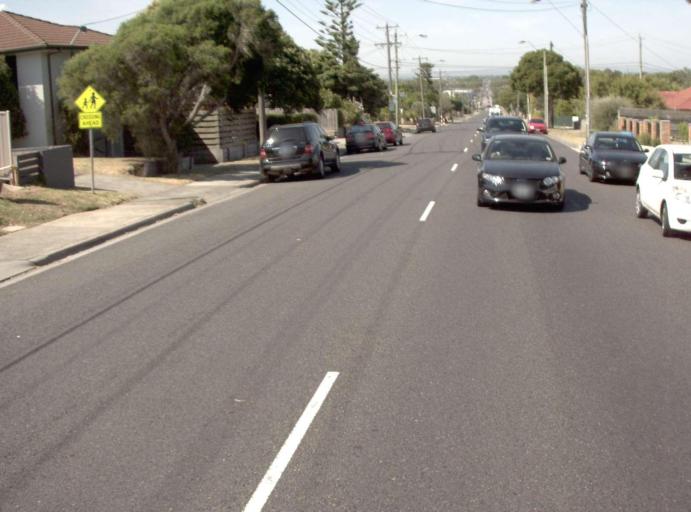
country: AU
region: Victoria
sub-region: Greater Dandenong
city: Noble Park North
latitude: -37.9685
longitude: 145.1868
